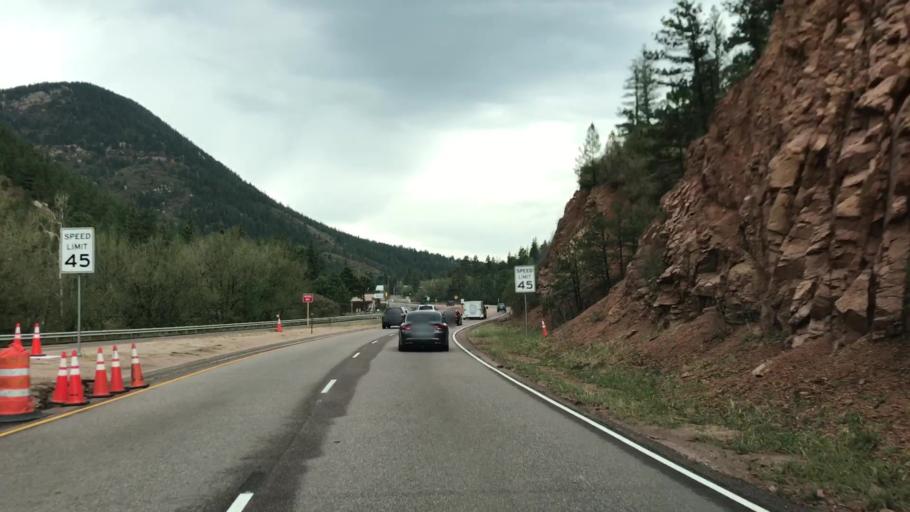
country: US
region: Colorado
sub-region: El Paso County
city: Manitou Springs
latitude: 38.8917
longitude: -104.9663
